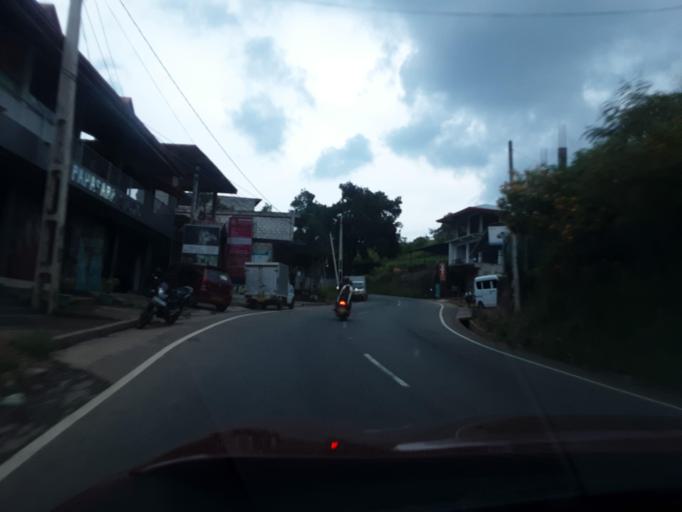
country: LK
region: Central
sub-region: Nuwara Eliya District
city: Nuwara Eliya
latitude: 6.9009
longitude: 80.9041
